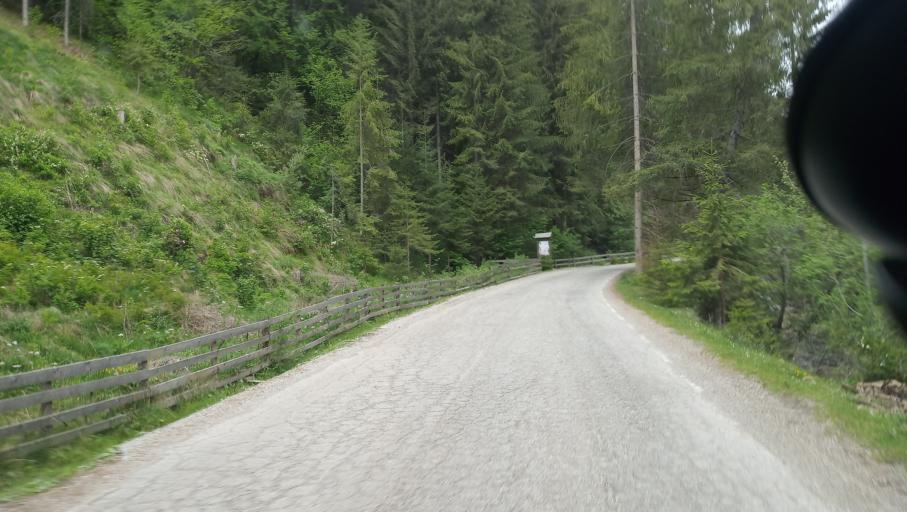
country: RO
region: Alba
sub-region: Comuna Horea
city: Horea
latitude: 46.5081
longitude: 22.9264
